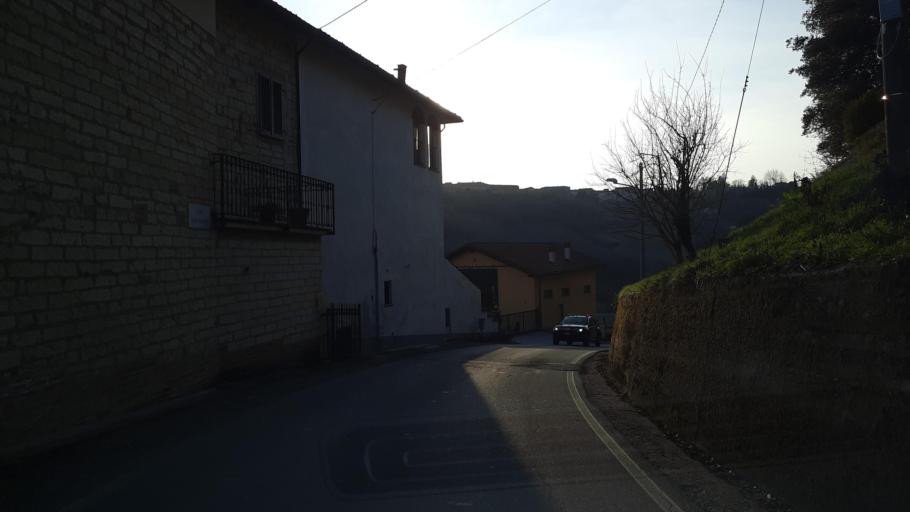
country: IT
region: Piedmont
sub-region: Provincia di Alessandria
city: Rosignano Monferrato
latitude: 45.0782
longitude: 8.3976
